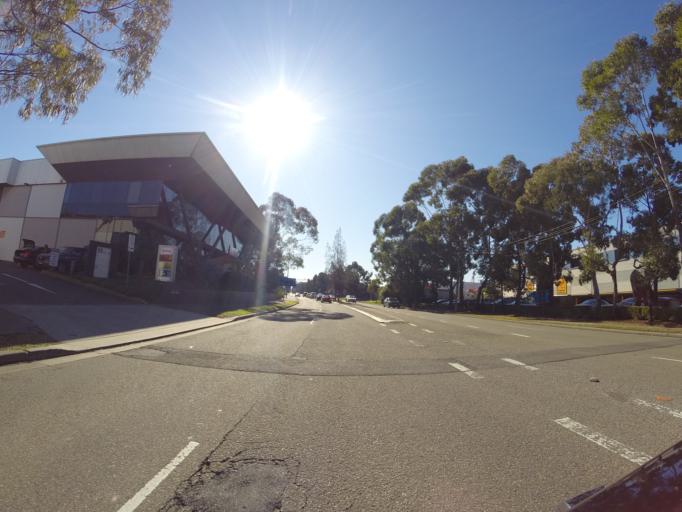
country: AU
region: New South Wales
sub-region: Auburn
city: Auburn
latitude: -33.8475
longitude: 151.0556
